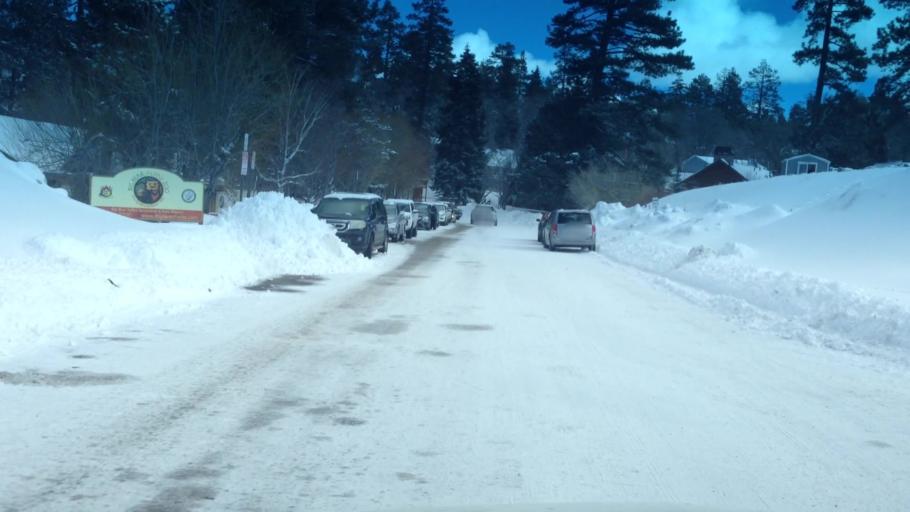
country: US
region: California
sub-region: San Bernardino County
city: Big Bear City
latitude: 34.2289
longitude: -116.8596
